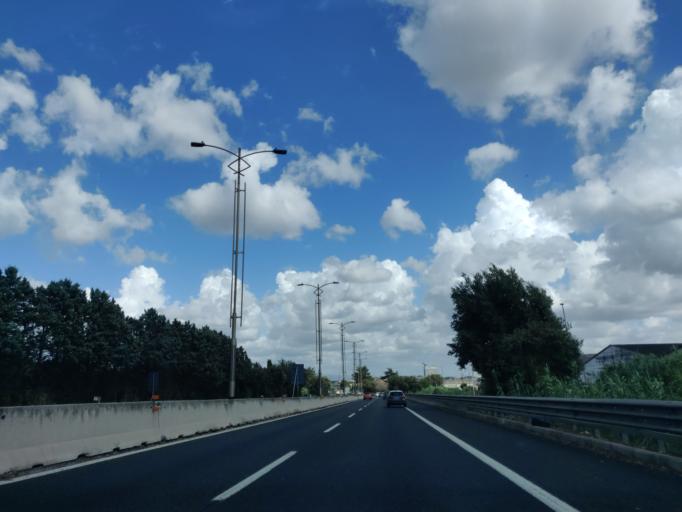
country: IT
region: Latium
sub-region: Citta metropolitana di Roma Capitale
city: Vitinia
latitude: 41.8328
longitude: 12.4313
